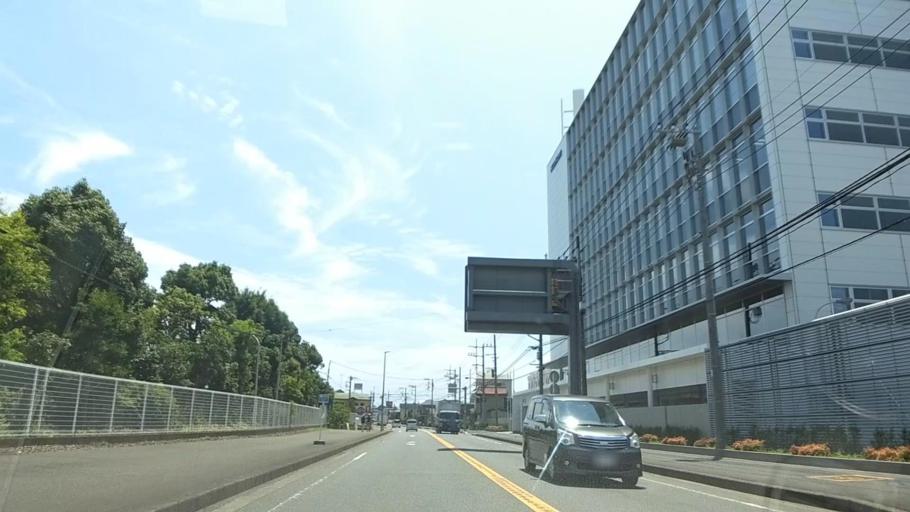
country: JP
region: Kanagawa
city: Atsugi
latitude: 35.3881
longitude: 139.3810
